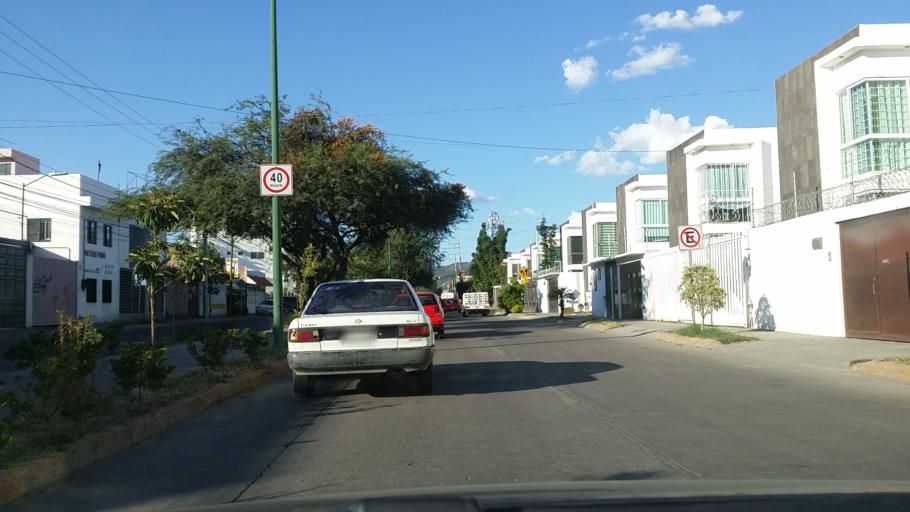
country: MX
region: Guanajuato
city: Leon
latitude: 21.1569
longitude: -101.6741
